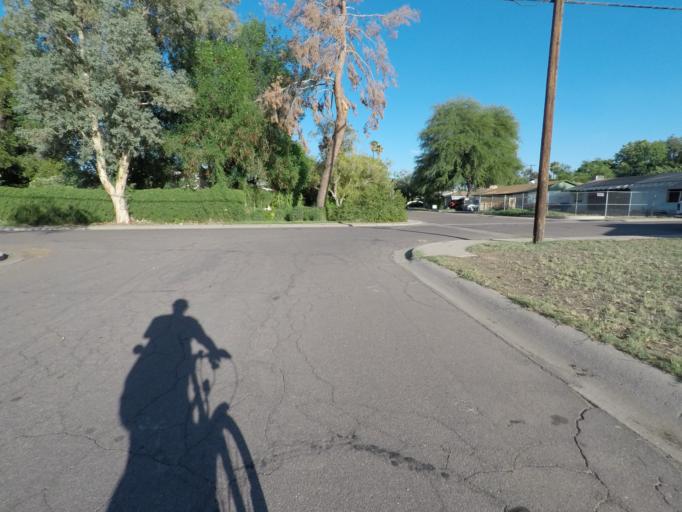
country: US
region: Arizona
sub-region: Maricopa County
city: Tempe Junction
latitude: 33.4179
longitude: -111.9487
